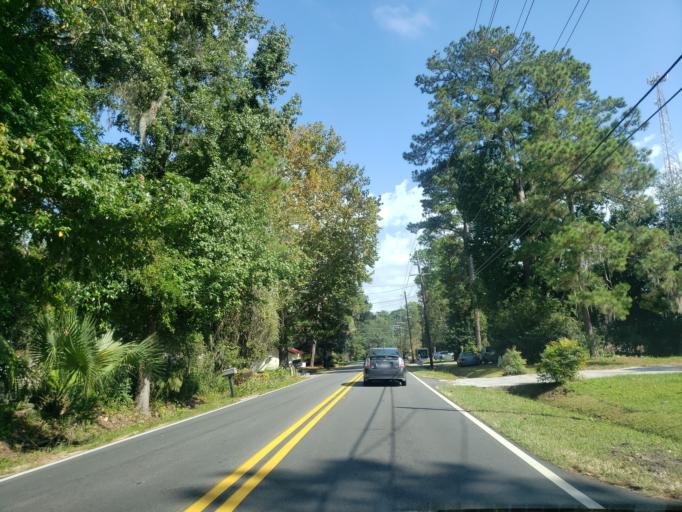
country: US
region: Georgia
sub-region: Chatham County
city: Montgomery
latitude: 31.9545
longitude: -81.1024
